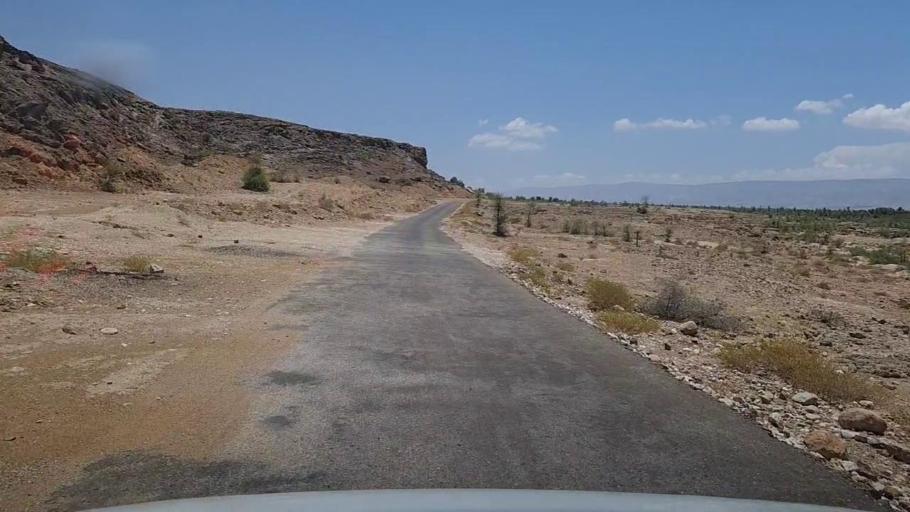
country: PK
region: Sindh
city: Bhan
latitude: 26.2898
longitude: 67.5330
